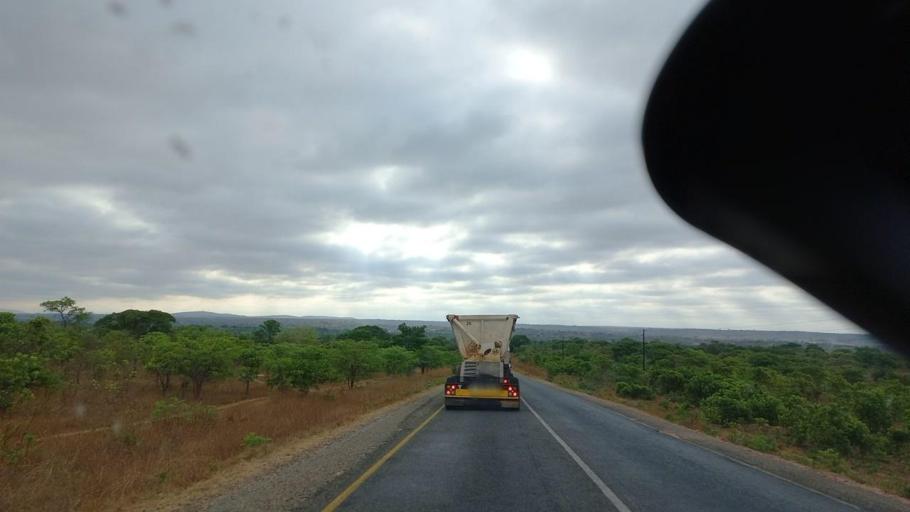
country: ZM
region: Lusaka
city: Chongwe
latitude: -15.2806
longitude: 28.7841
